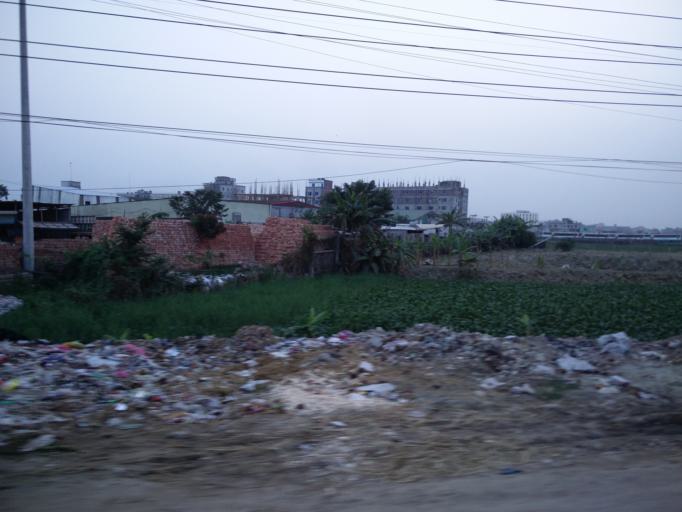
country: BD
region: Dhaka
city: Azimpur
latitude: 23.7959
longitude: 90.2651
